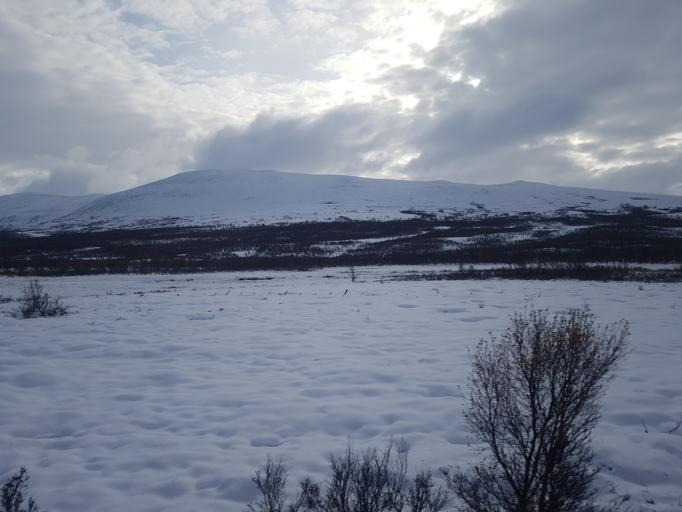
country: NO
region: Oppland
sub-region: Dovre
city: Dovre
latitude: 62.1281
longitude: 9.3088
